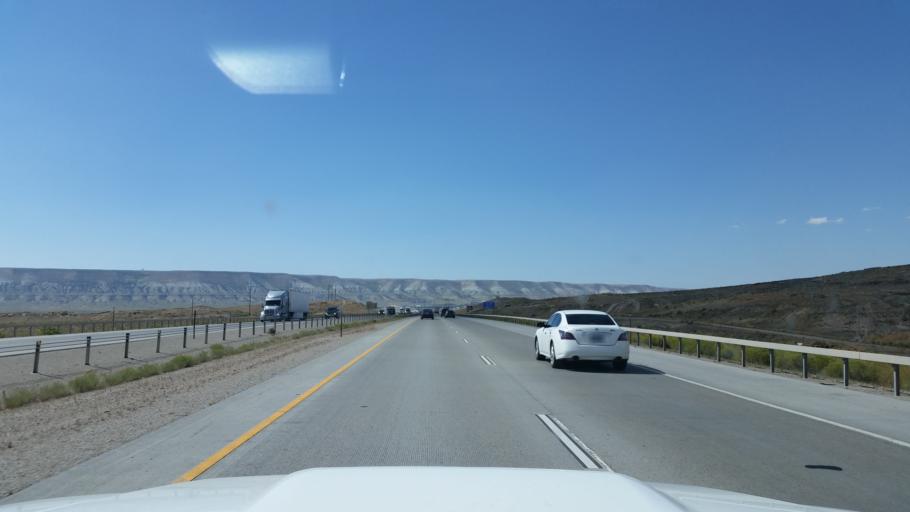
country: US
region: Wyoming
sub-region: Sweetwater County
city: Rock Springs
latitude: 41.6059
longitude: -109.2079
